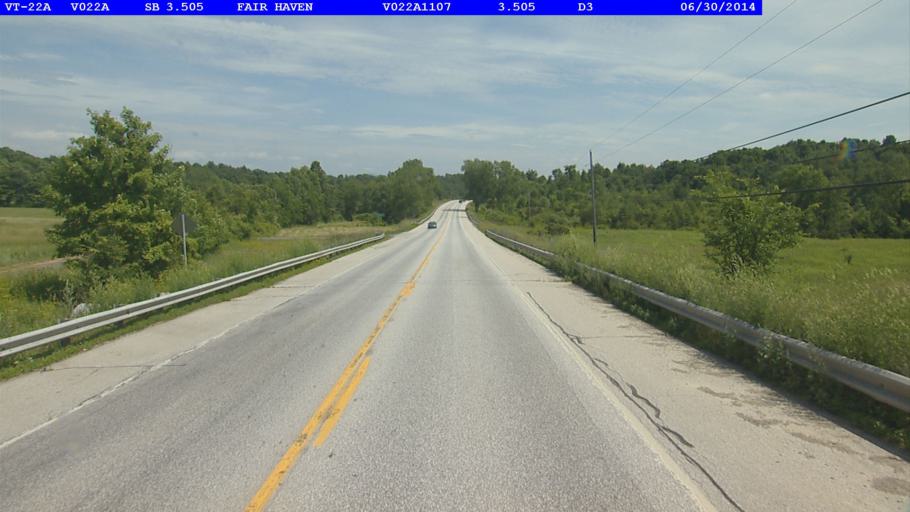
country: US
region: Vermont
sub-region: Rutland County
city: Fair Haven
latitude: 43.6156
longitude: -73.2933
